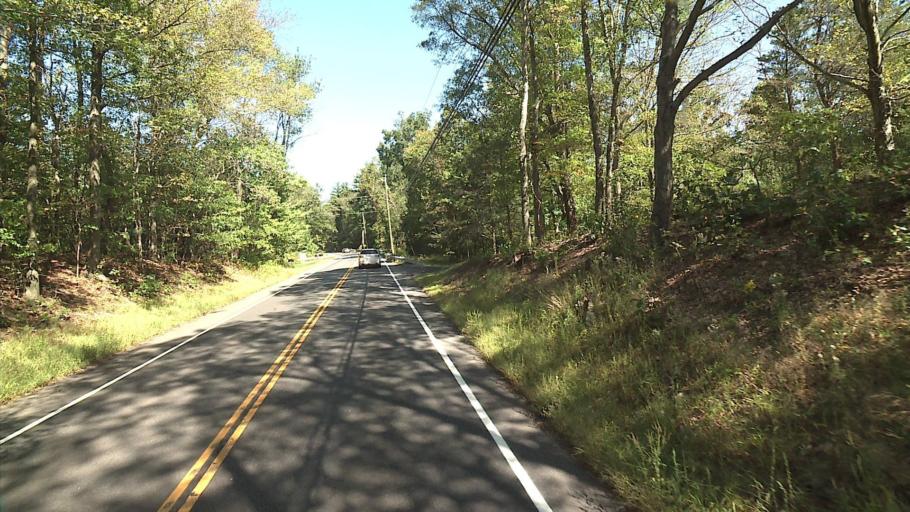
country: US
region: Connecticut
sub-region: New Haven County
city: Prospect
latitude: 41.4504
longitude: -72.9688
